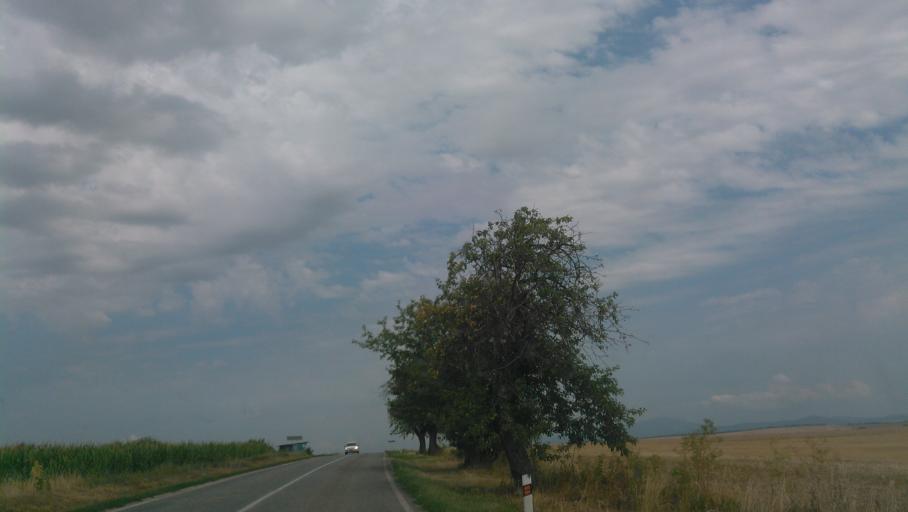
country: SK
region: Trnavsky
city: Hlohovec
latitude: 48.4554
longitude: 17.9267
